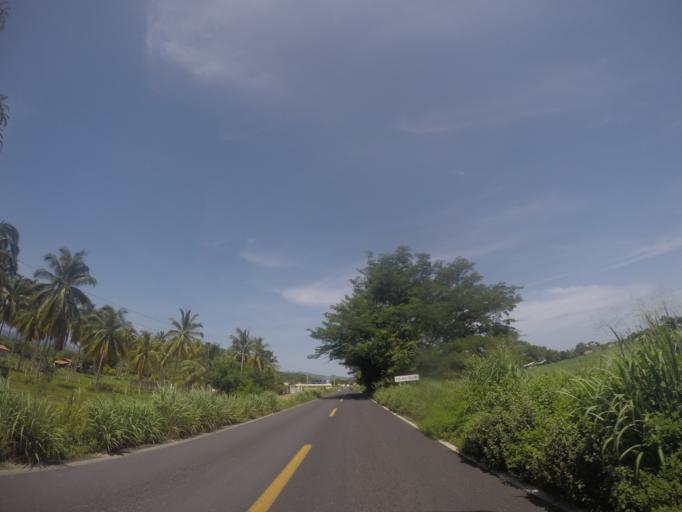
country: MX
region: Oaxaca
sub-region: Villa de Tututepec de Melchor Ocampo
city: Santa Rosa de Lima
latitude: 16.0113
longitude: -97.4553
